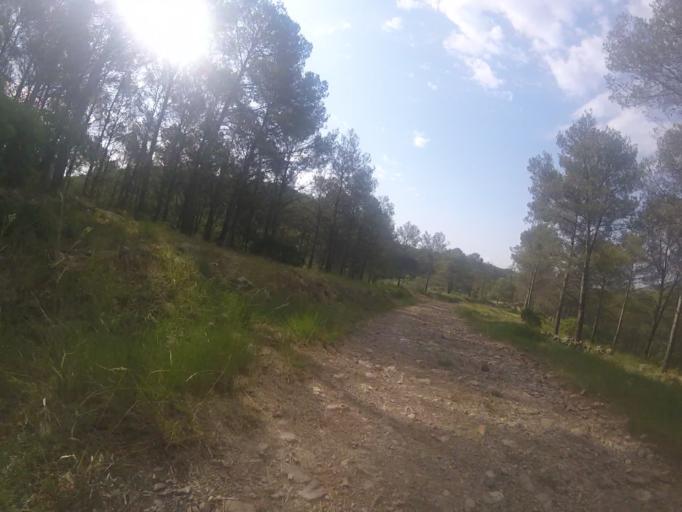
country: ES
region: Valencia
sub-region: Provincia de Castello
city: Cervera del Maestre
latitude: 40.4000
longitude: 0.2053
